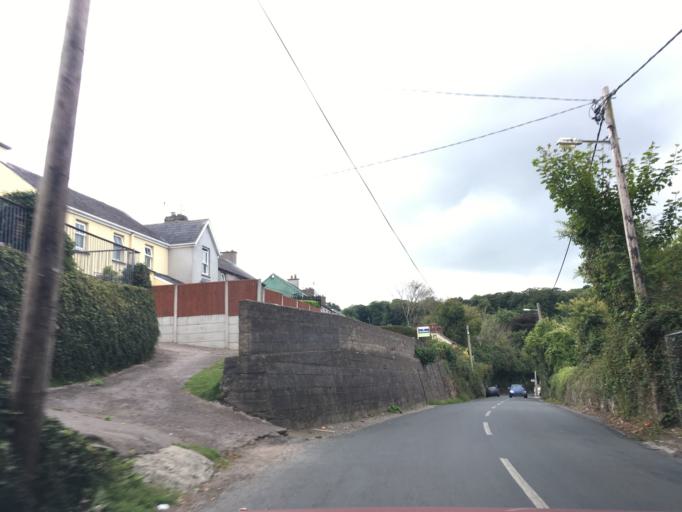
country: IE
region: Munster
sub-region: County Cork
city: Crosshaven
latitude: 51.8026
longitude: -8.2926
